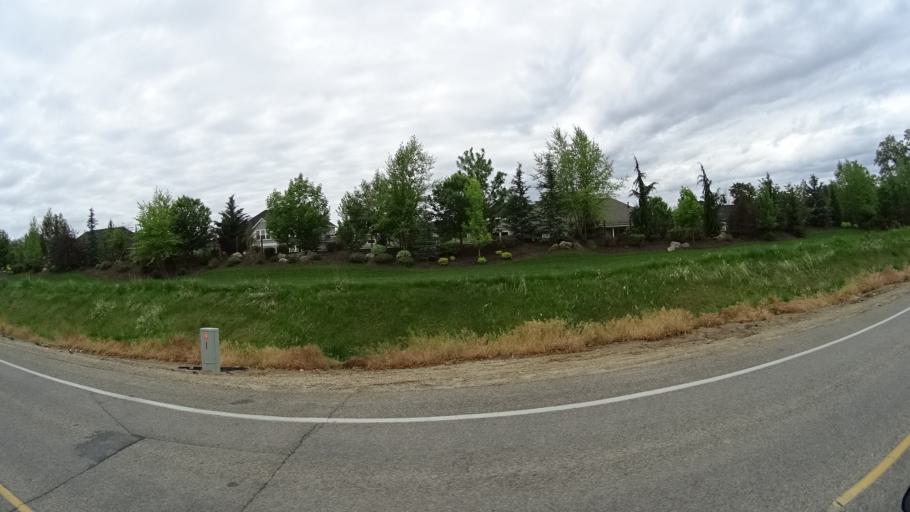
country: US
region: Idaho
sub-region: Ada County
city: Eagle
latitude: 43.7064
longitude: -116.3814
